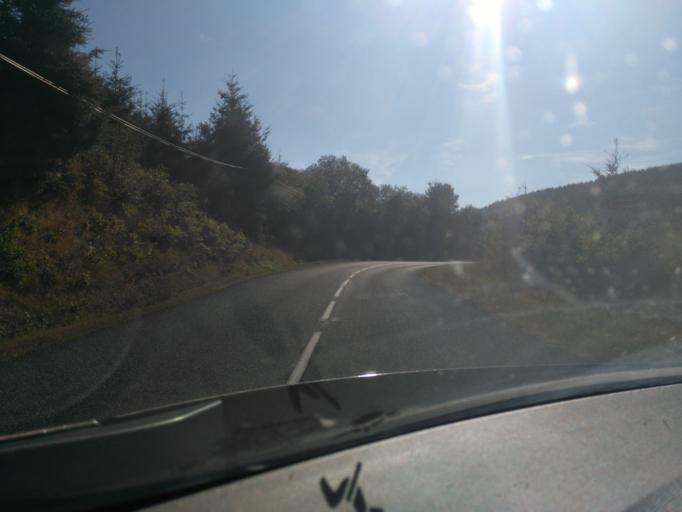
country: FR
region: Rhone-Alpes
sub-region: Departement de la Loire
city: Violay
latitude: 45.8484
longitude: 4.4021
